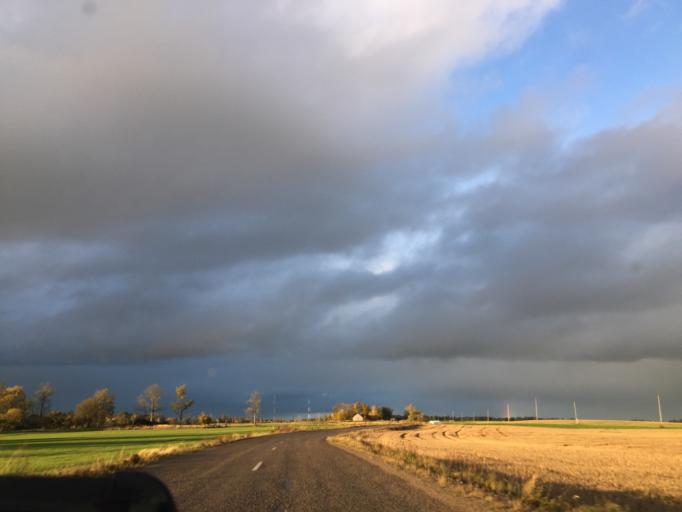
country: LV
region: Talsu Rajons
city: Sabile
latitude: 56.9290
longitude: 22.3960
